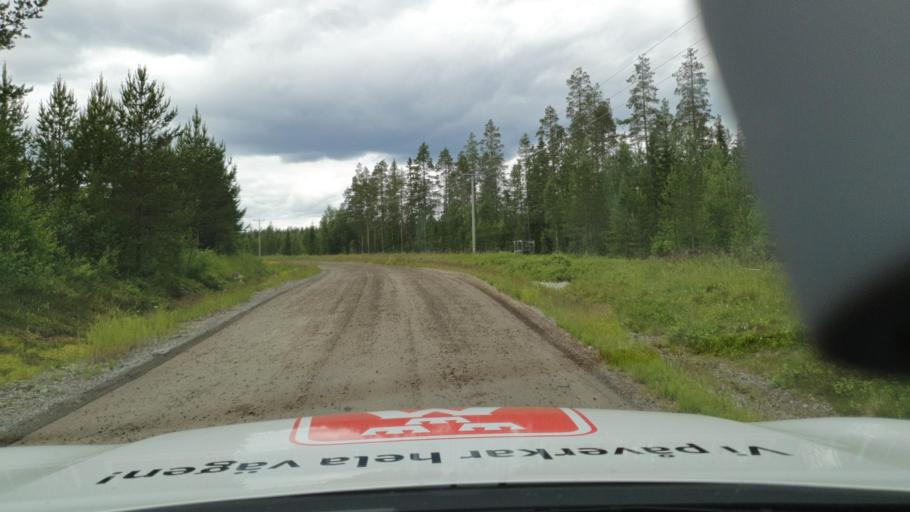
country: SE
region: Vaesterbotten
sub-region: Bjurholms Kommun
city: Bjurholm
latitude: 63.8079
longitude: 19.0733
